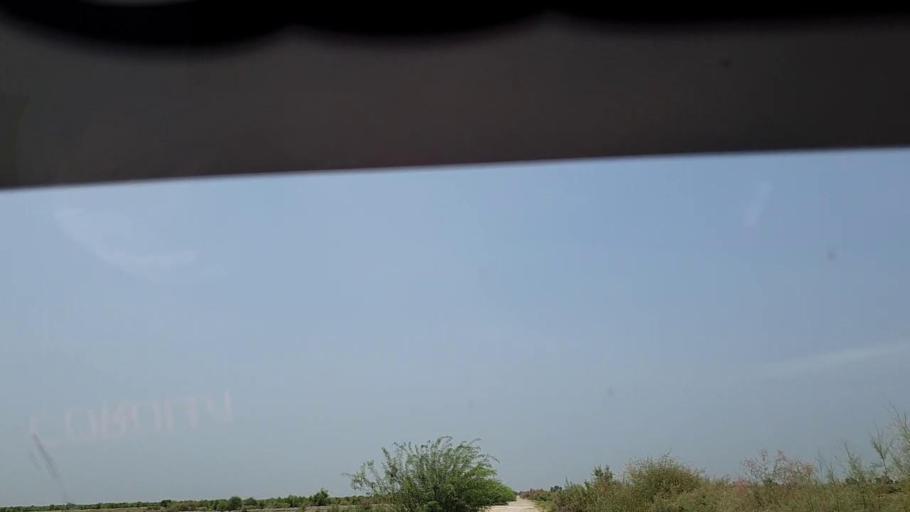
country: PK
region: Sindh
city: Adilpur
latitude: 27.8881
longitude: 69.2555
